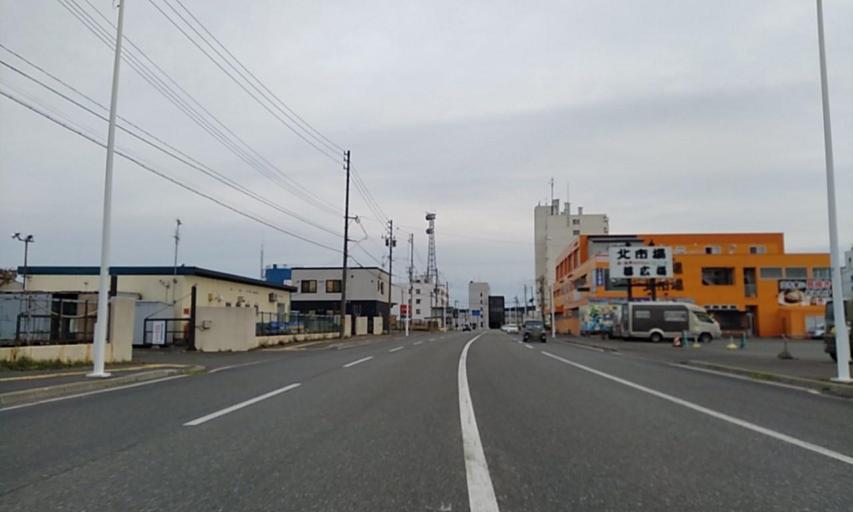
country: JP
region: Hokkaido
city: Wakkanai
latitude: 45.4176
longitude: 141.6779
